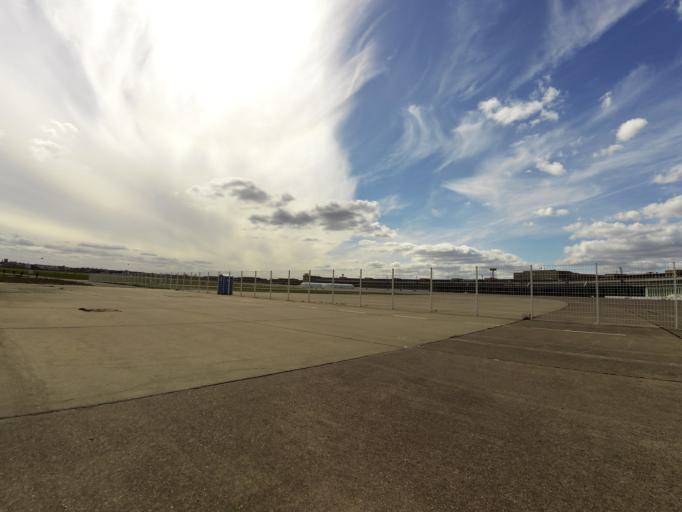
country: DE
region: Berlin
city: Tempelhof Bezirk
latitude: 52.4812
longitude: 13.3989
